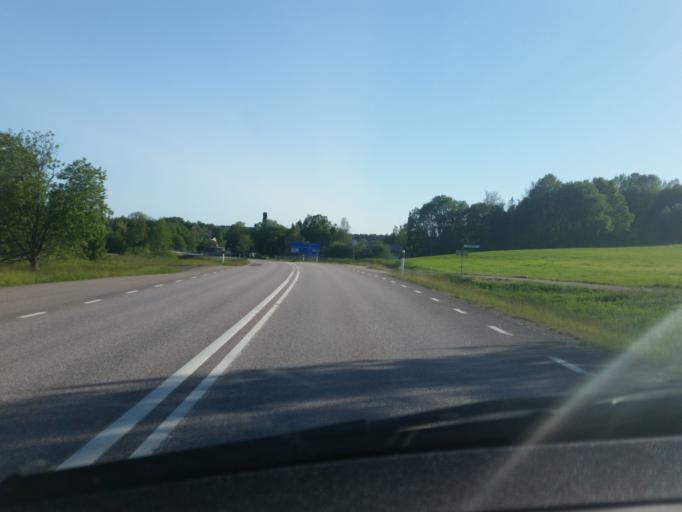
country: SE
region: Vaestra Goetaland
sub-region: Fargelanda Kommun
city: Faergelanda
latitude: 58.5757
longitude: 12.0083
